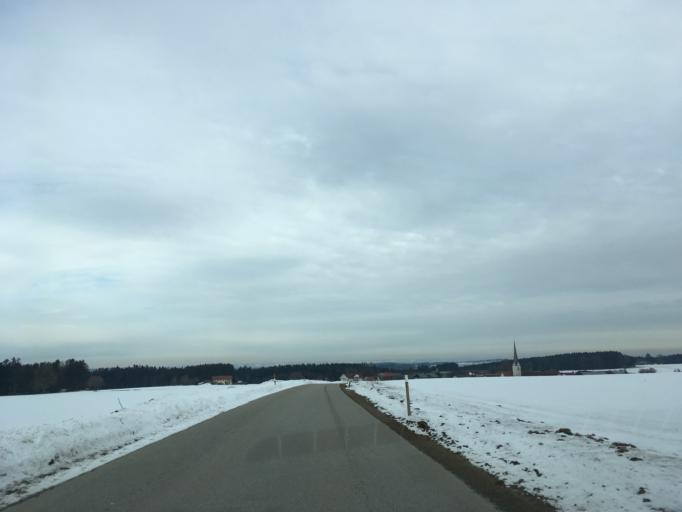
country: DE
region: Bavaria
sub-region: Upper Bavaria
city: Unterreit
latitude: 48.1071
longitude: 12.3707
